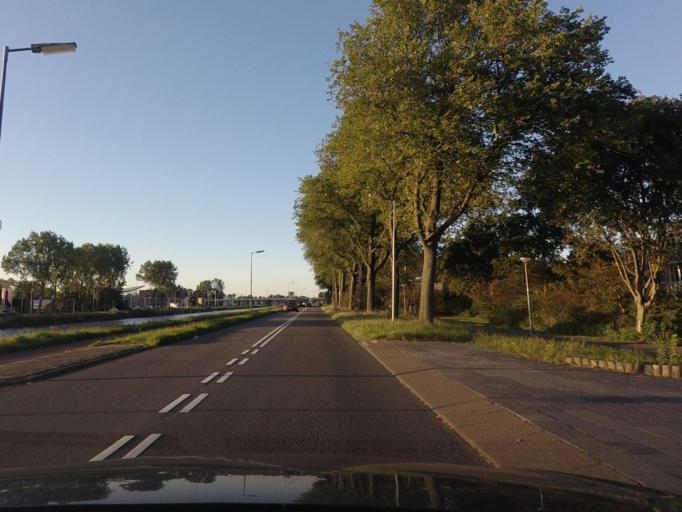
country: NL
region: North Holland
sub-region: Gemeente Alkmaar
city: Alkmaar
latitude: 52.6430
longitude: 4.7456
